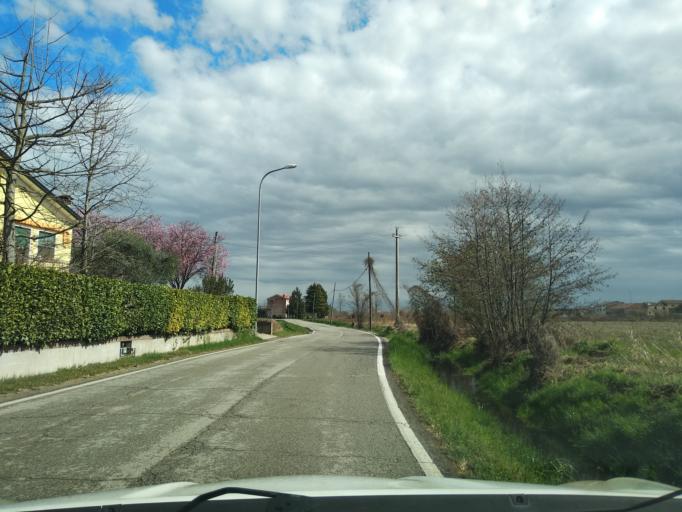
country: IT
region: Veneto
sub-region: Provincia di Vicenza
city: Vigardolo
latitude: 45.6074
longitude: 11.5937
